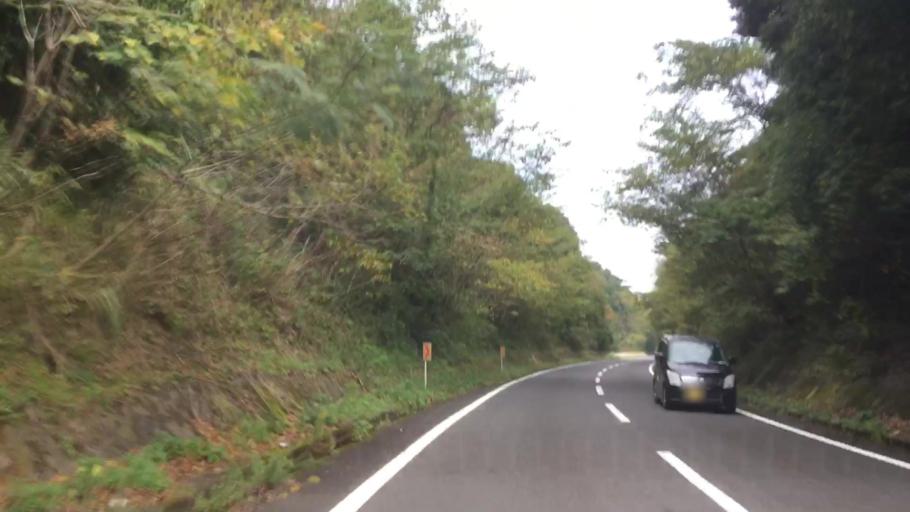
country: JP
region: Nagasaki
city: Sasebo
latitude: 32.9993
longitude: 129.7075
